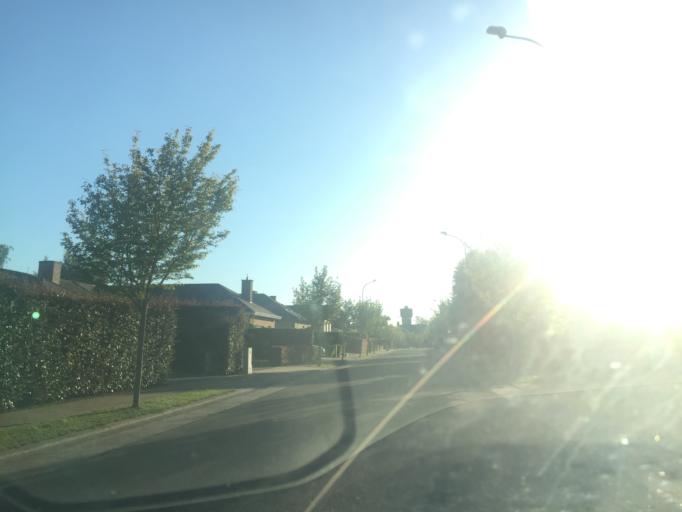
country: BE
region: Flanders
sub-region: Provincie West-Vlaanderen
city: Izegem
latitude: 50.9101
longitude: 3.2255
